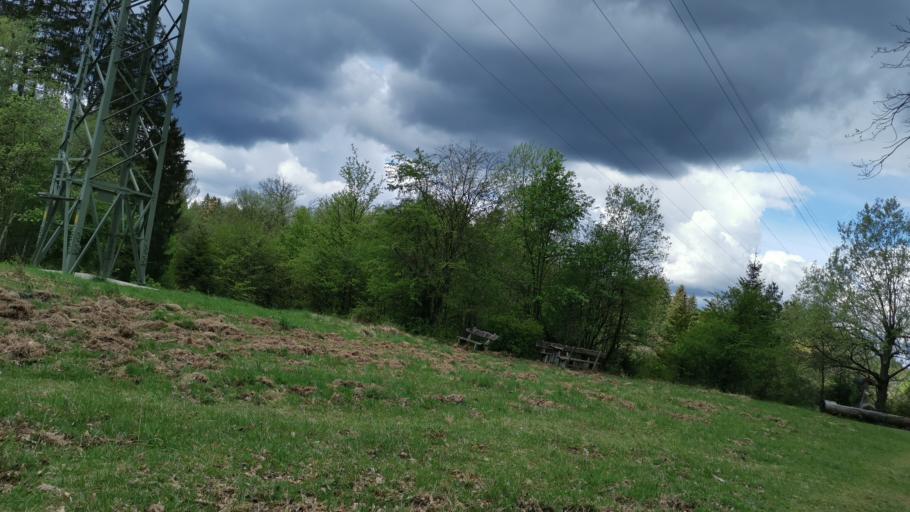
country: DE
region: Bavaria
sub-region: Upper Bavaria
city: Baierbrunn
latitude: 48.0466
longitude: 11.4728
